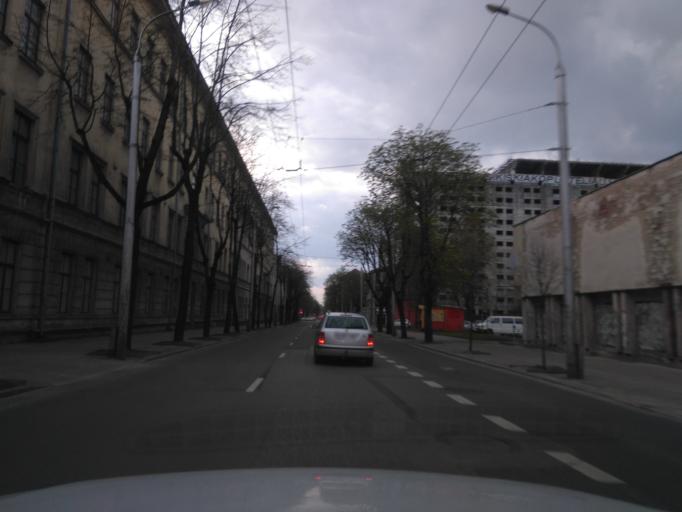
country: LT
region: Kauno apskritis
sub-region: Kaunas
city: Kaunas
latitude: 54.8954
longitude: 23.9209
